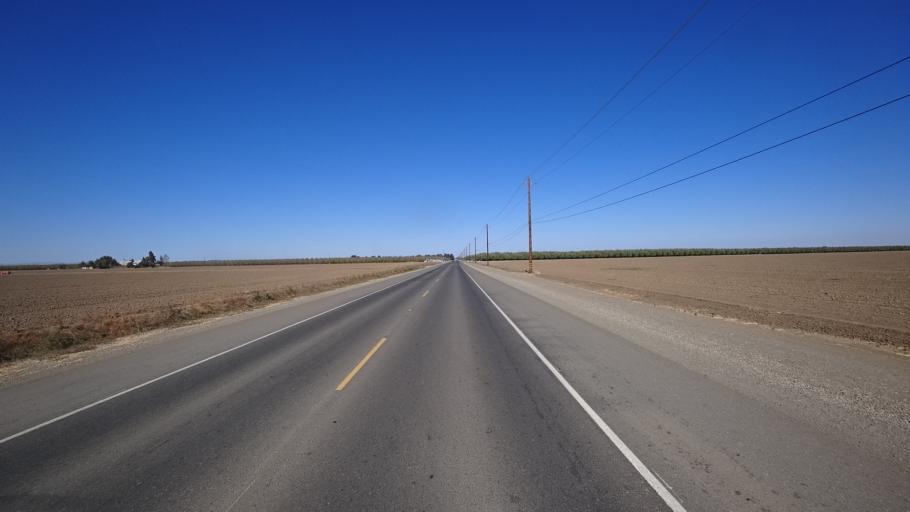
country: US
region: California
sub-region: Yolo County
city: Davis
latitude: 38.5949
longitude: -121.8034
